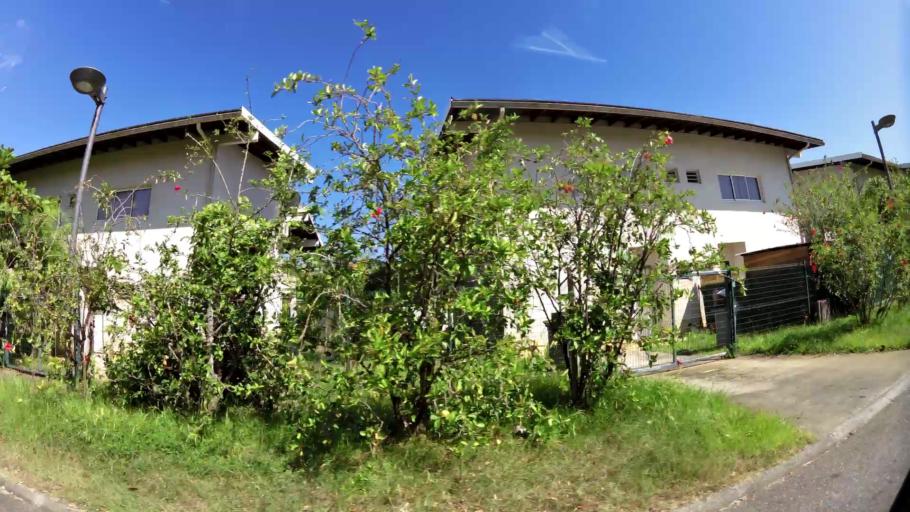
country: GF
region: Guyane
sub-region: Guyane
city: Remire-Montjoly
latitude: 4.9157
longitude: -52.2762
